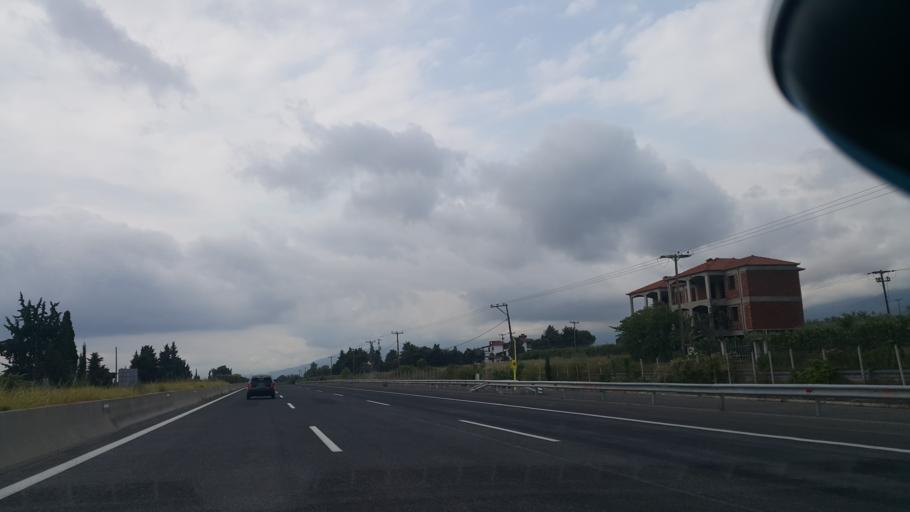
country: GR
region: Central Macedonia
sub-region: Nomos Pierias
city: Leptokarya
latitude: 40.1160
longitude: 22.5526
